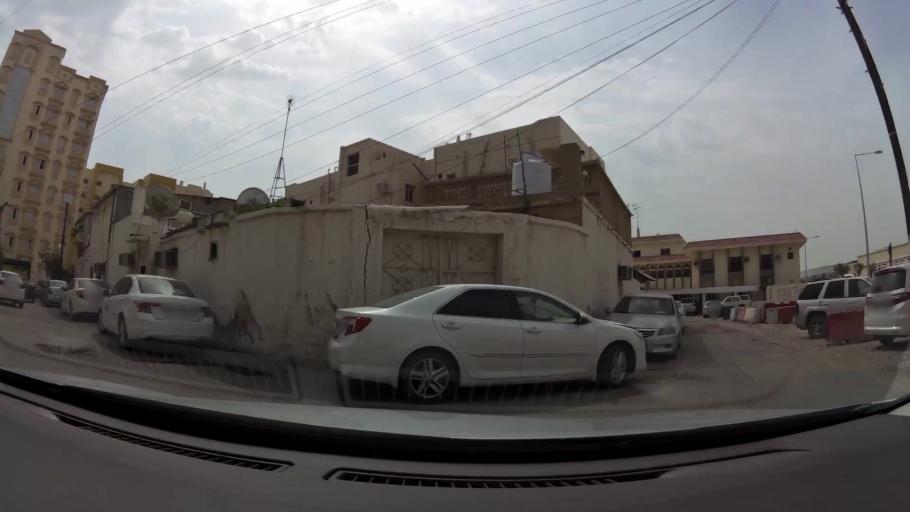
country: QA
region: Baladiyat ad Dawhah
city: Doha
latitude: 25.2845
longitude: 51.5002
